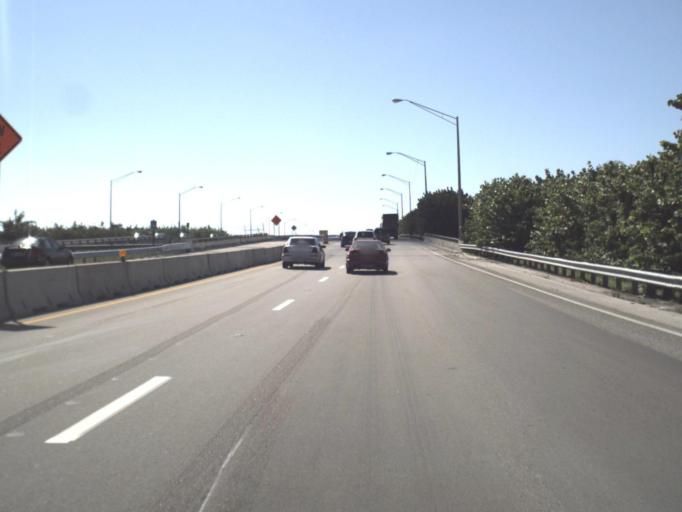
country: US
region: Florida
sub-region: Miami-Dade County
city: Cutler Ridge
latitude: 25.5694
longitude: -80.3632
